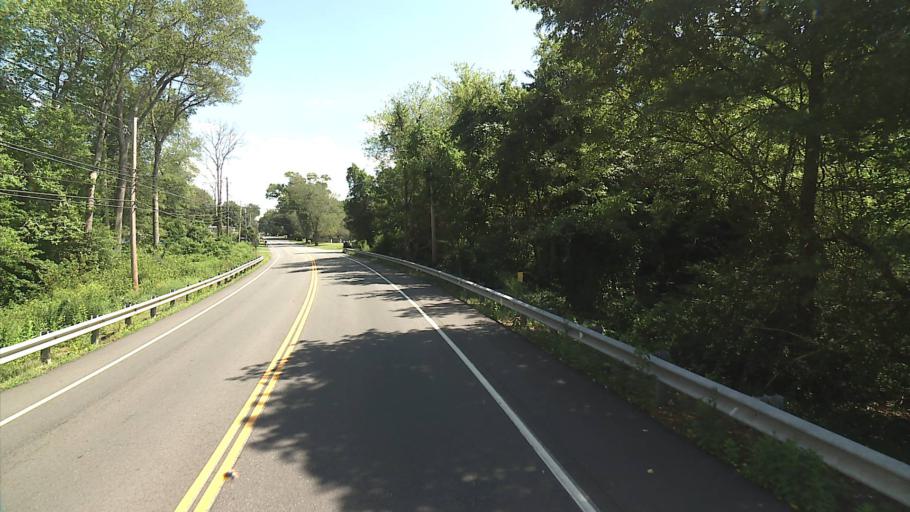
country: US
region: Connecticut
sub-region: Middlesex County
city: Old Saybrook Center
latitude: 41.3347
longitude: -72.3148
